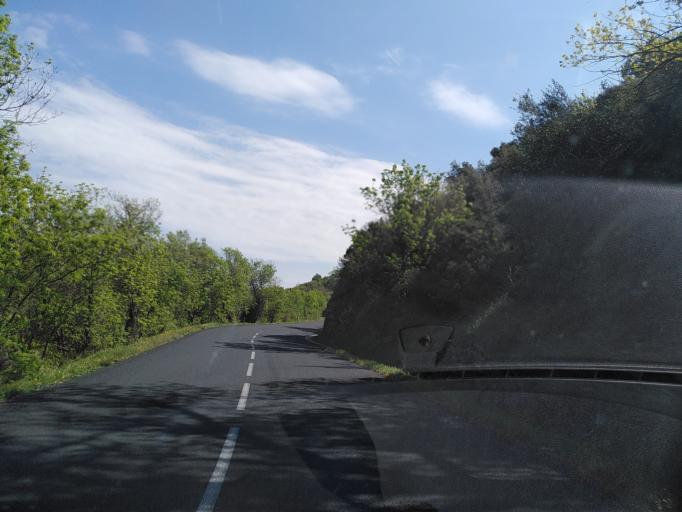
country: FR
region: Languedoc-Roussillon
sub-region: Departement de l'Aude
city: Portel-des-Corbieres
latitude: 42.9922
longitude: 2.7947
